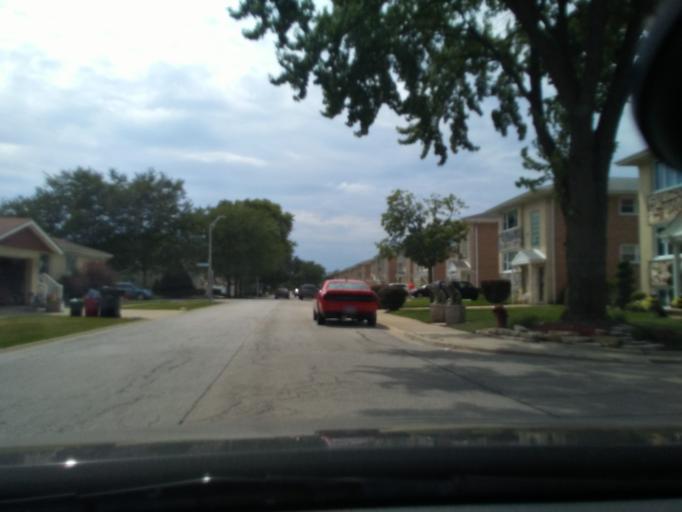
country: US
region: Illinois
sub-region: Cook County
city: Norridge
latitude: 41.9702
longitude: -87.8384
